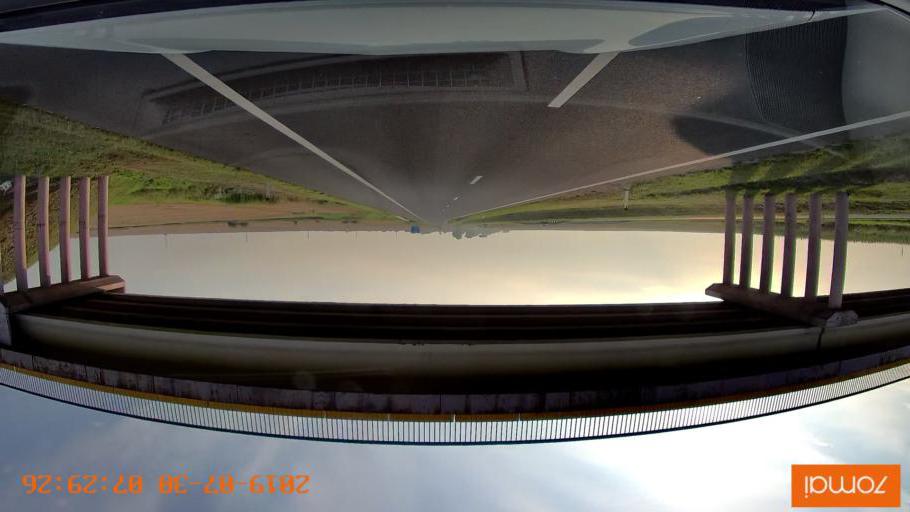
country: RU
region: Kaliningrad
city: Gvardeysk
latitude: 54.6722
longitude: 20.9395
